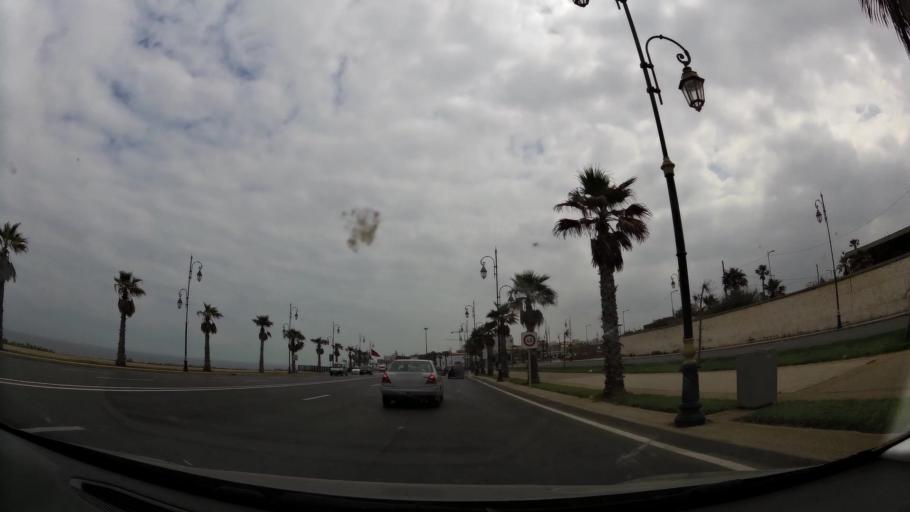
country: MA
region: Rabat-Sale-Zemmour-Zaer
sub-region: Rabat
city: Rabat
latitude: 34.0069
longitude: -6.8684
